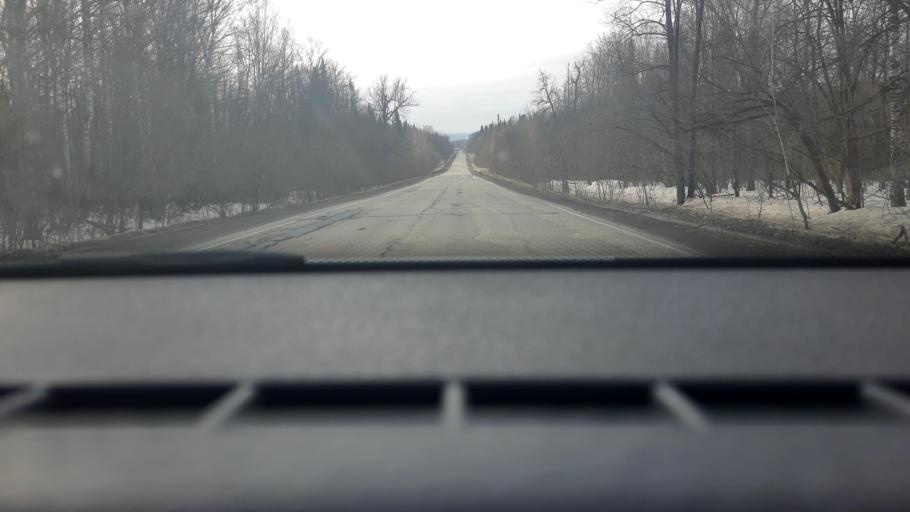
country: RU
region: Chelyabinsk
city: Asha
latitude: 54.9030
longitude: 57.2962
